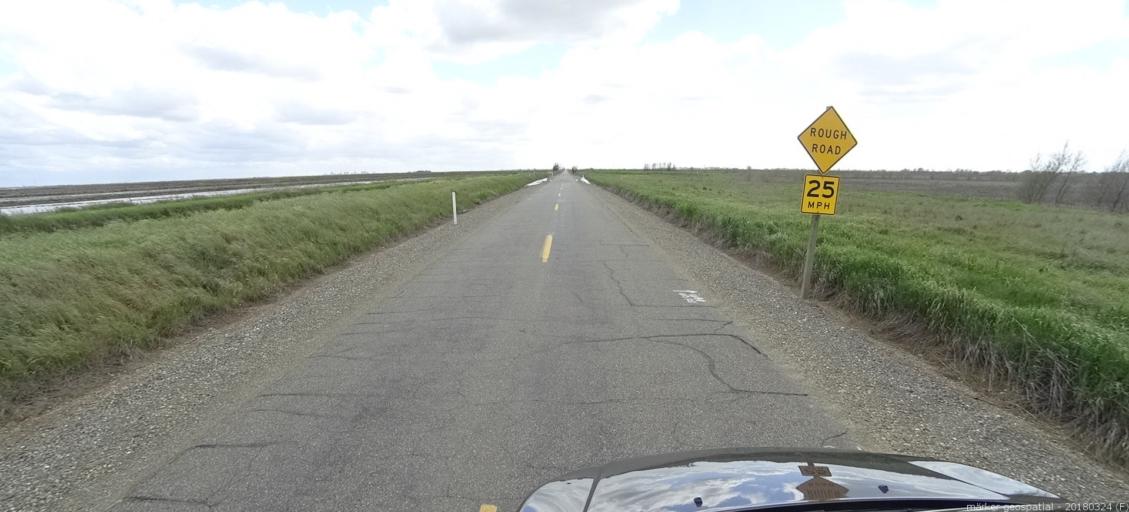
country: US
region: California
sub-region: Sacramento County
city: Elverta
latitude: 38.7355
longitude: -121.5768
